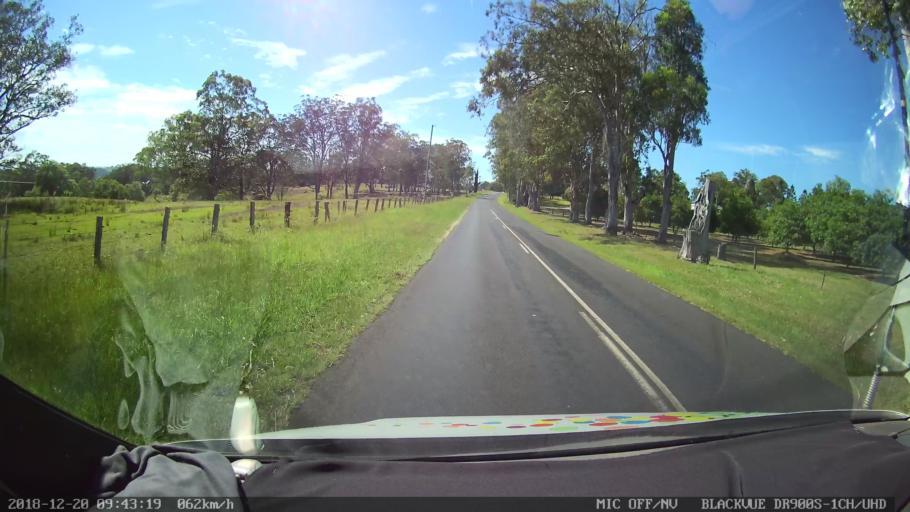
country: AU
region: New South Wales
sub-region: Lismore Municipality
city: Lismore
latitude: -28.7247
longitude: 153.2954
